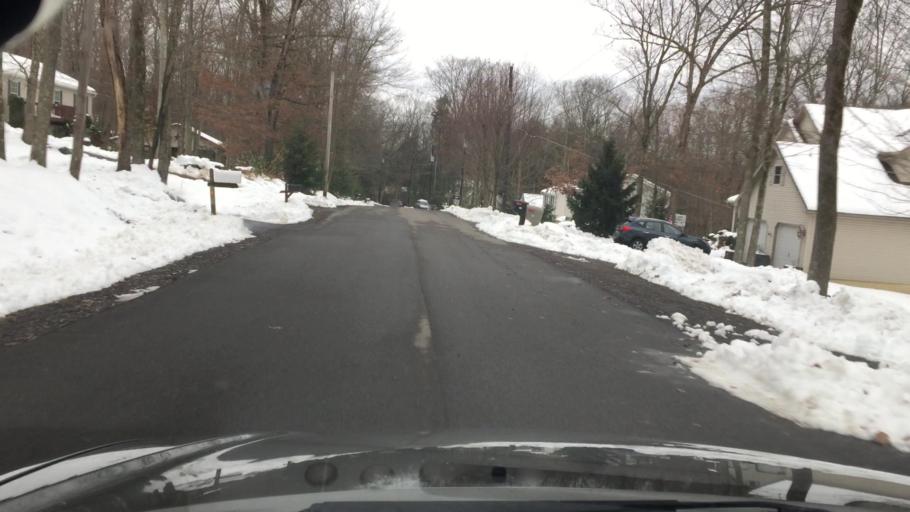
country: US
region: Pennsylvania
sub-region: Luzerne County
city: Freeland
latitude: 41.0364
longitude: -75.9380
